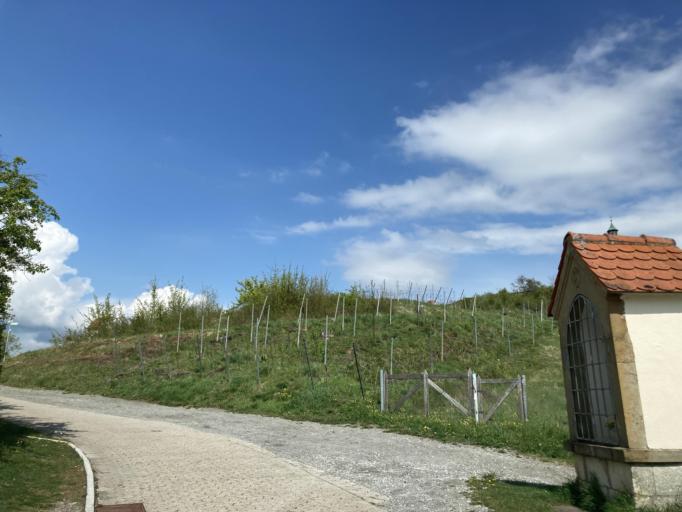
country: DE
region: Baden-Wuerttemberg
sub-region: Tuebingen Region
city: Rottenburg
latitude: 48.5061
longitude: 8.9800
